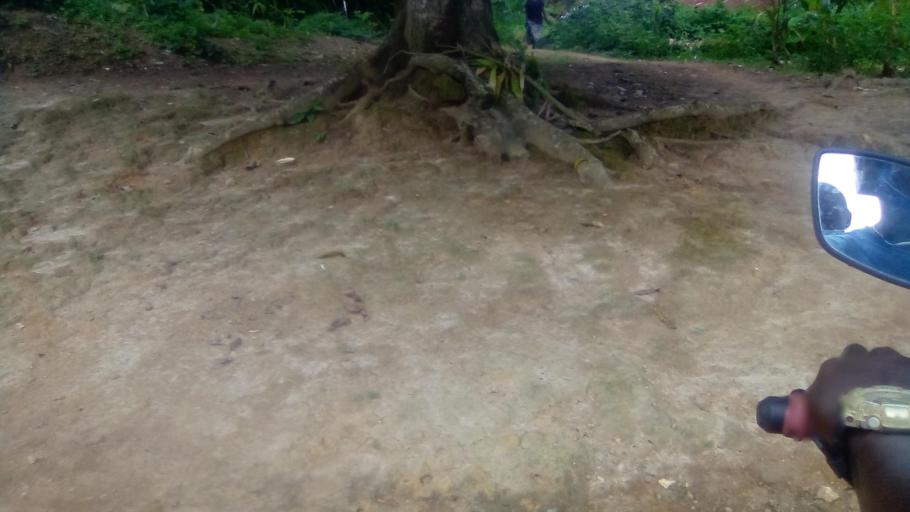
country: SL
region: Eastern Province
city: Kailahun
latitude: 8.2829
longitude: -10.5716
